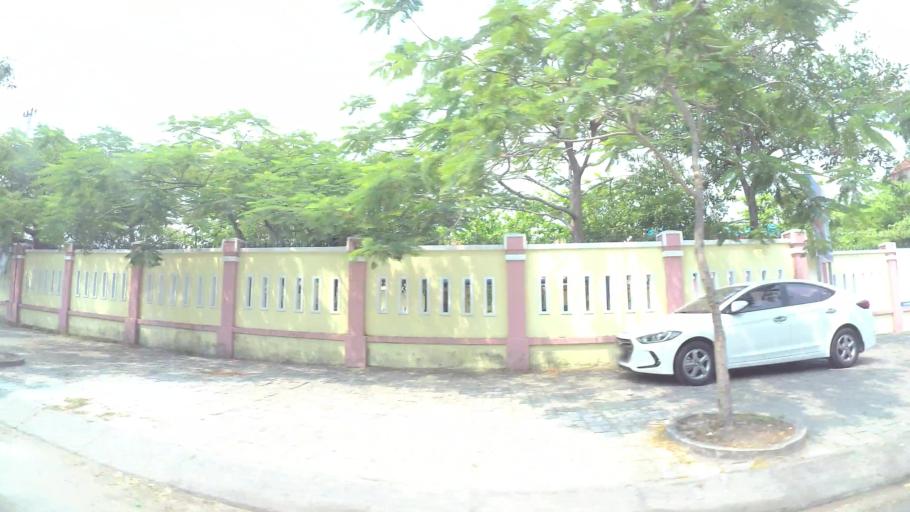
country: VN
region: Da Nang
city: Da Nang
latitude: 16.0867
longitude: 108.2309
